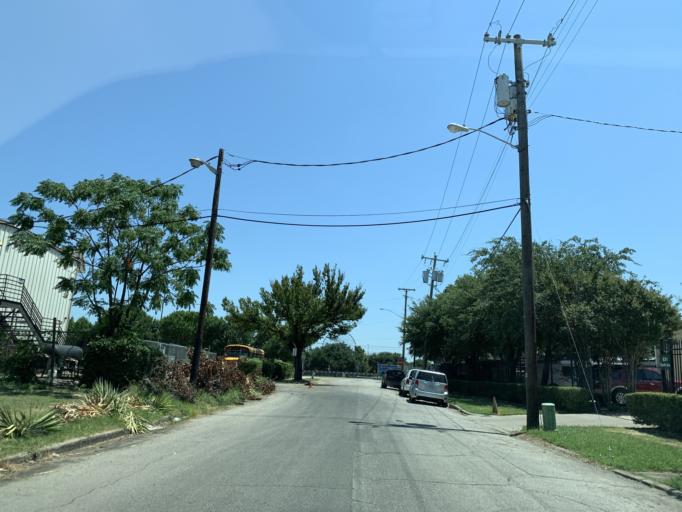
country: US
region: Texas
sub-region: Dallas County
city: Dallas
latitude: 32.7789
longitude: -96.7686
